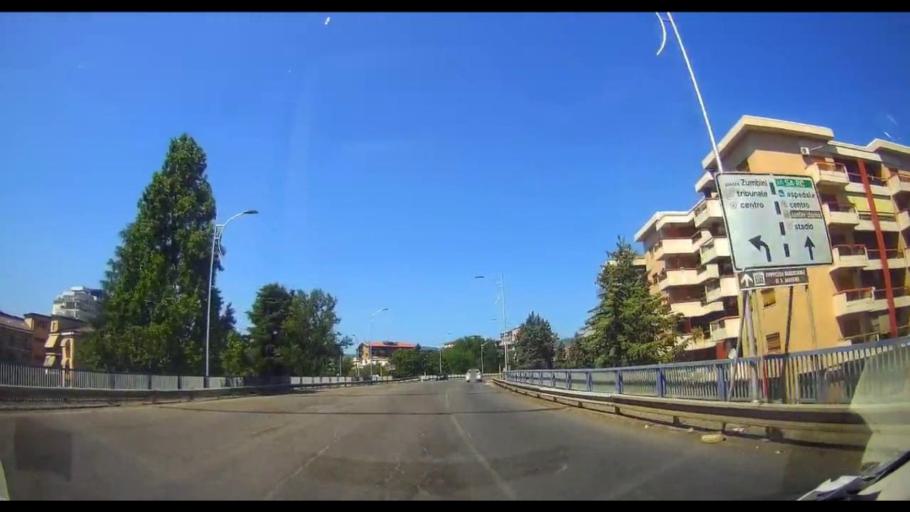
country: IT
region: Calabria
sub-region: Provincia di Cosenza
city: Cosenza
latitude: 39.3107
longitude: 16.2530
